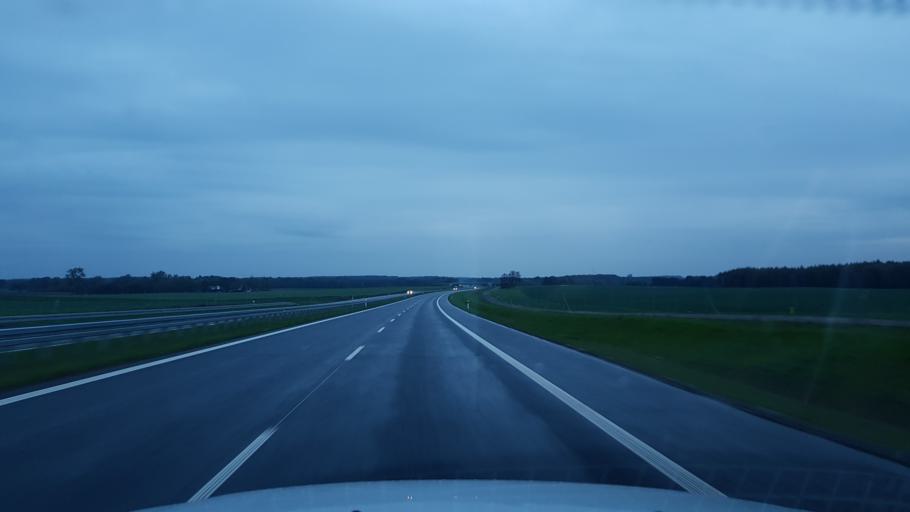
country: PL
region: West Pomeranian Voivodeship
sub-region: Powiat gryficki
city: Brojce
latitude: 53.9182
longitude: 15.3832
